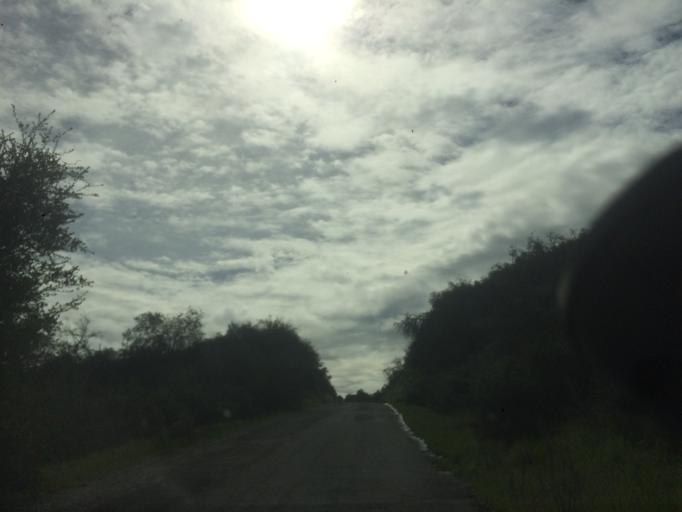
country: US
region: California
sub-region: San Luis Obispo County
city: Nipomo
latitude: 35.2049
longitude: -120.4478
